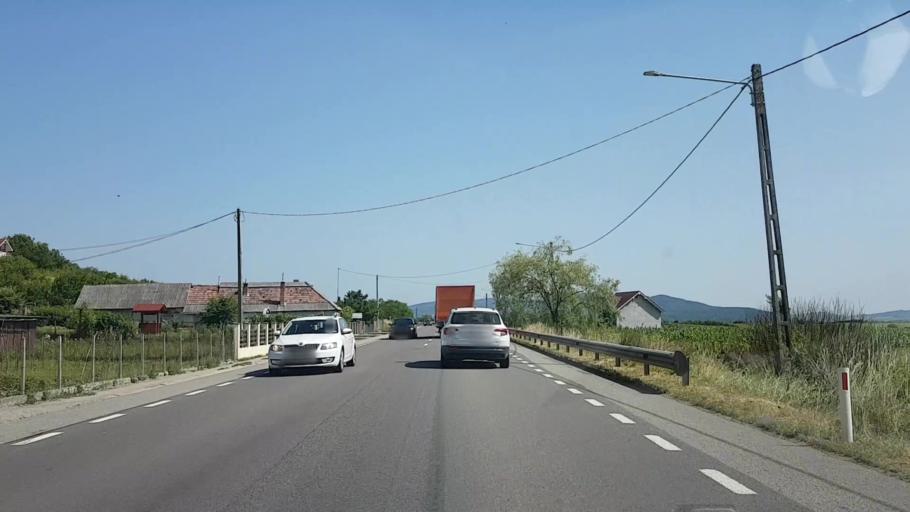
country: RO
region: Bistrita-Nasaud
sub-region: Comuna Sieu-Odorhei
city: Sieu-Odorhei
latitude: 47.1330
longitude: 24.3101
